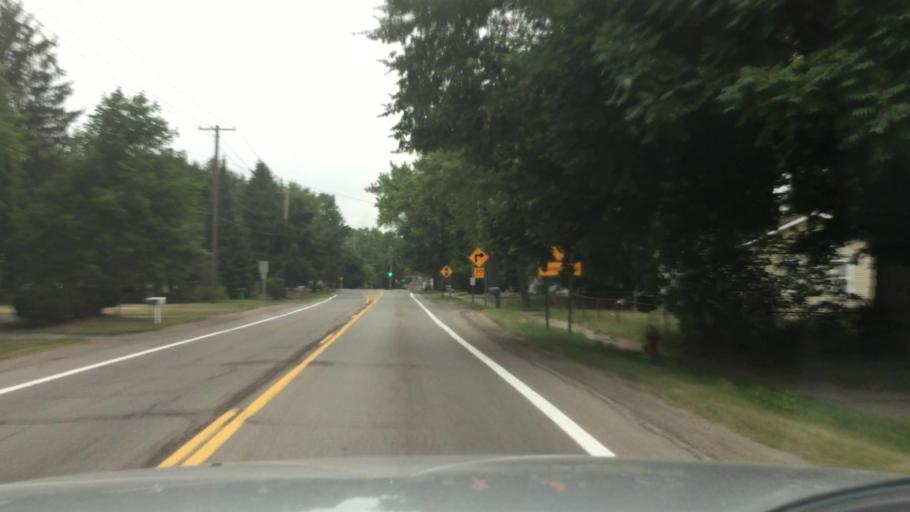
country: US
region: Michigan
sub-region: Oakland County
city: Waterford
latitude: 42.6785
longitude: -83.4316
